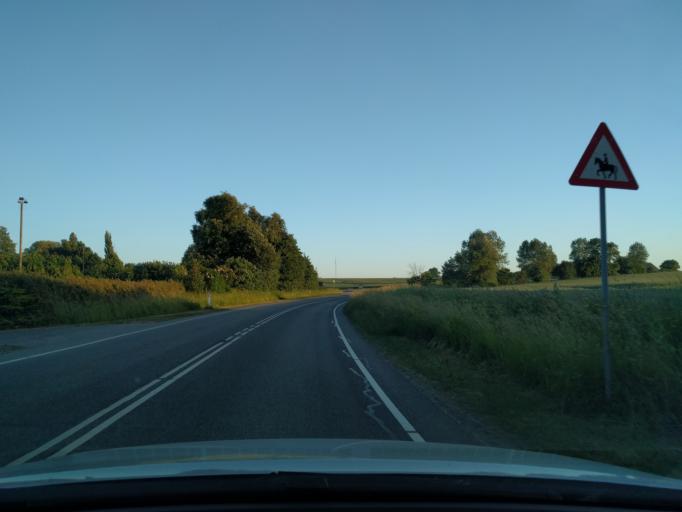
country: DK
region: South Denmark
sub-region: Kerteminde Kommune
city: Munkebo
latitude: 55.4685
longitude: 10.6004
